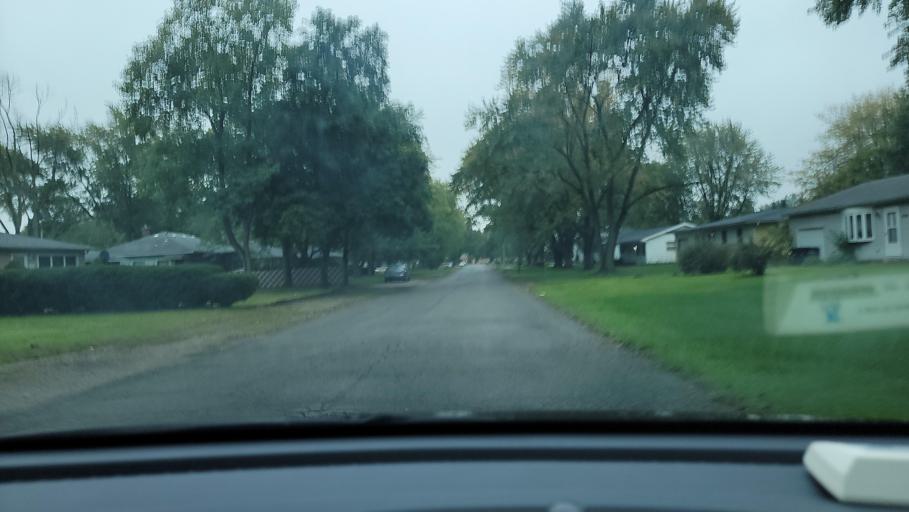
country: US
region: Indiana
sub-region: Porter County
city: Portage
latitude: 41.5715
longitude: -87.1814
